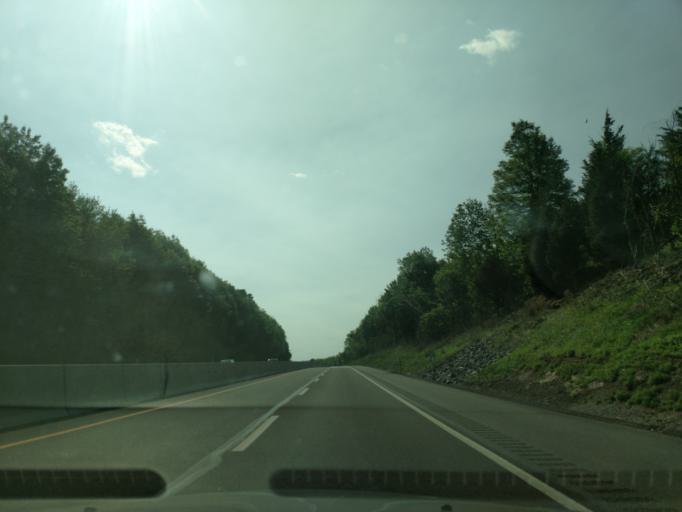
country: US
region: Pennsylvania
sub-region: Lancaster County
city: Denver
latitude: 40.2431
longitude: -76.1521
